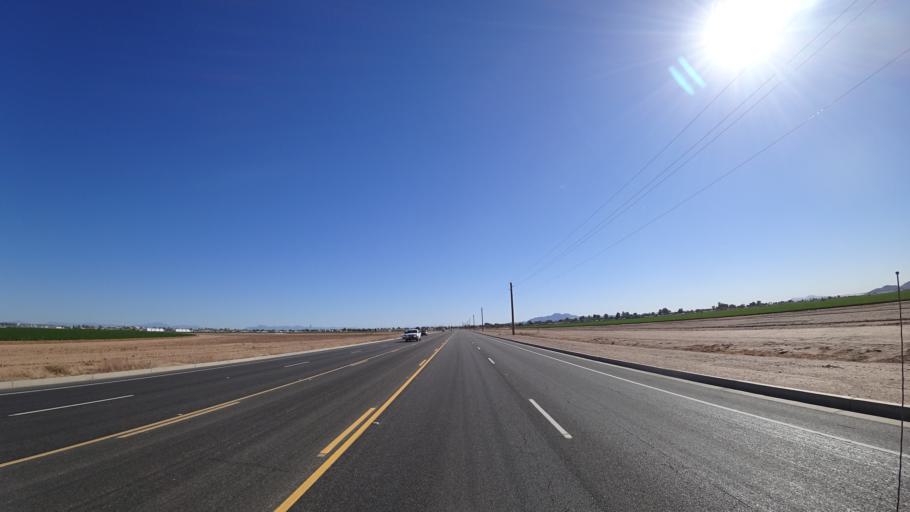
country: US
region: Arizona
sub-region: Maricopa County
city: Sun Lakes
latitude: 33.2192
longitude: -111.9046
